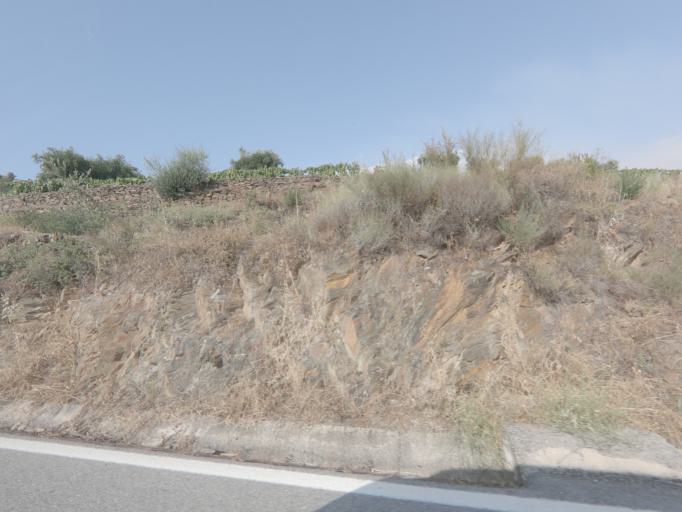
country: PT
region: Viseu
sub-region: Tabuaco
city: Tabuaco
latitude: 41.1390
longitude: -7.5377
